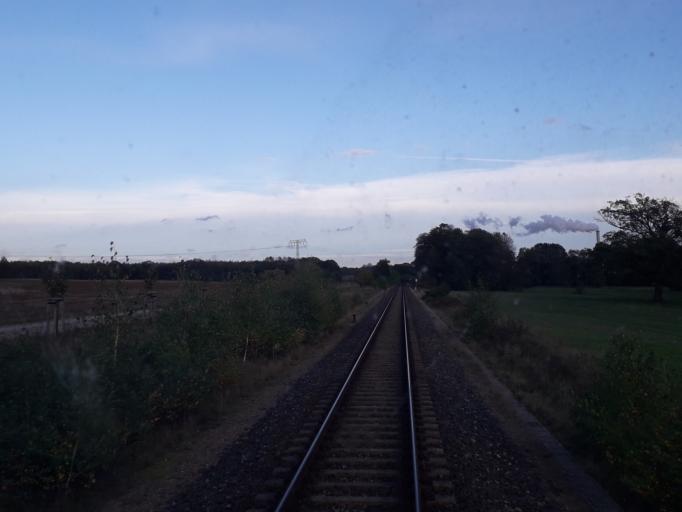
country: DE
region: Brandenburg
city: Heiligengrabe
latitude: 53.1529
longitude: 12.3621
